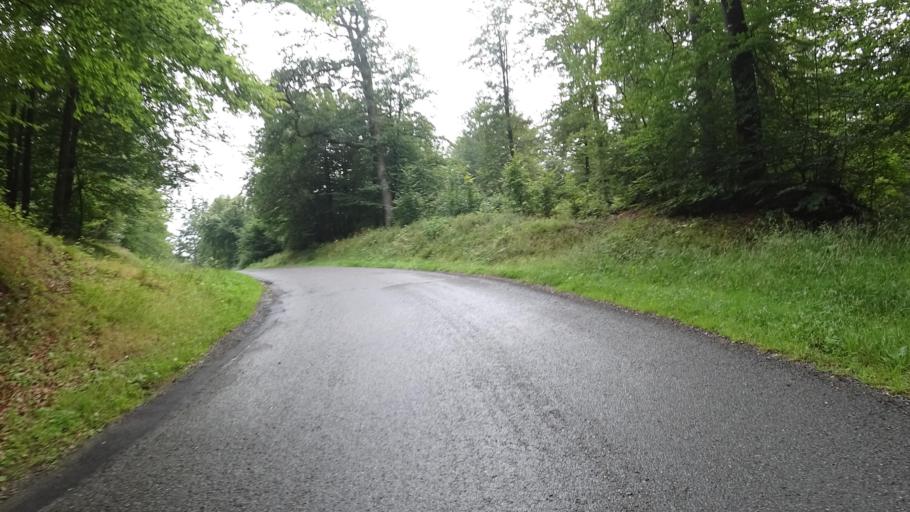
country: BE
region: Wallonia
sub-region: Province du Luxembourg
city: Chiny
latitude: 49.7774
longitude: 5.3635
